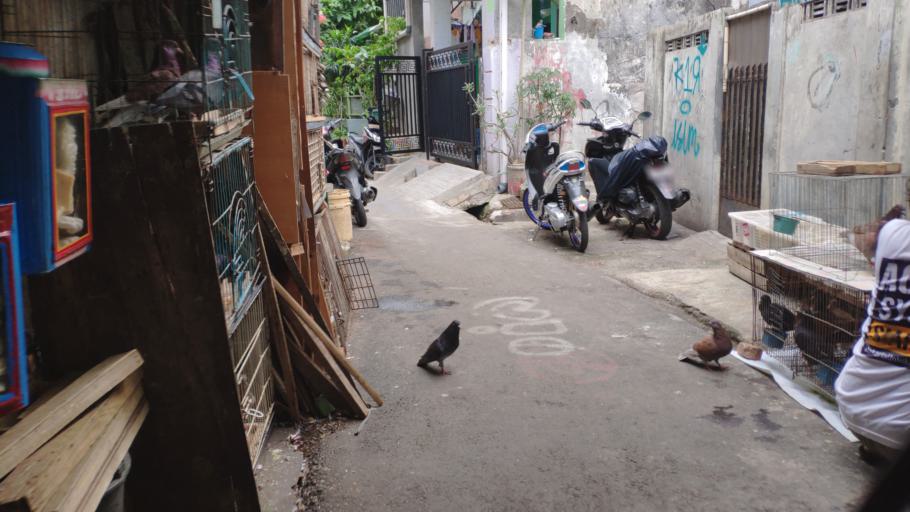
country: ID
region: Jakarta Raya
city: Jakarta
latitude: -6.2149
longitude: 106.8662
